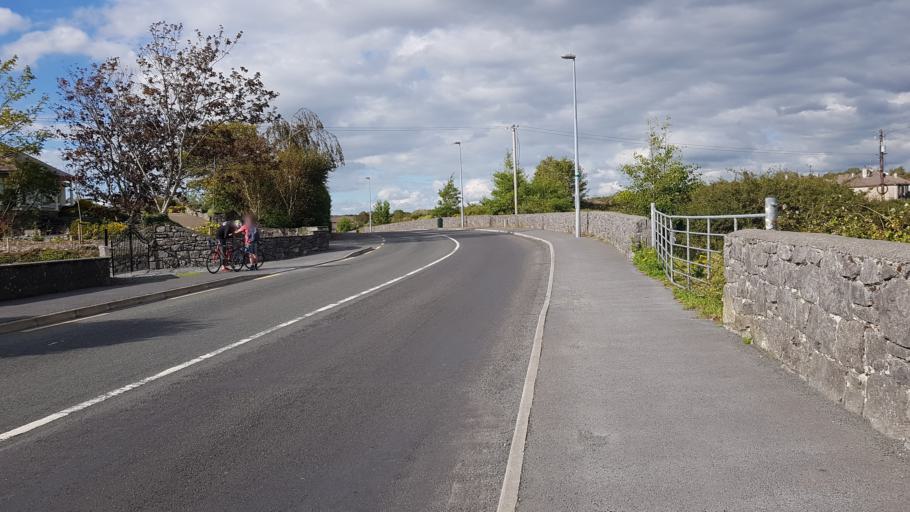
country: IE
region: Connaught
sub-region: County Galway
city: Gaillimh
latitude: 53.2902
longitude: -9.0518
